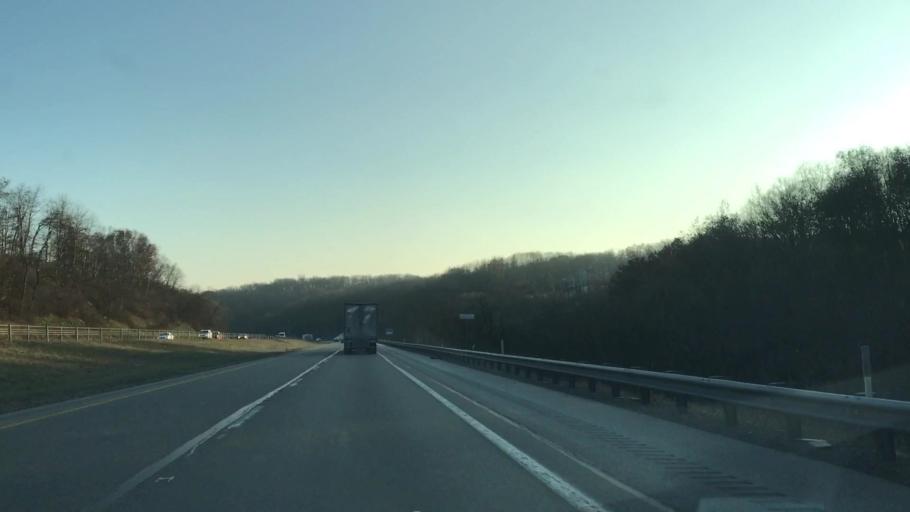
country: US
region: Pennsylvania
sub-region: Allegheny County
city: Franklin Park
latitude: 40.5756
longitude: -80.1177
